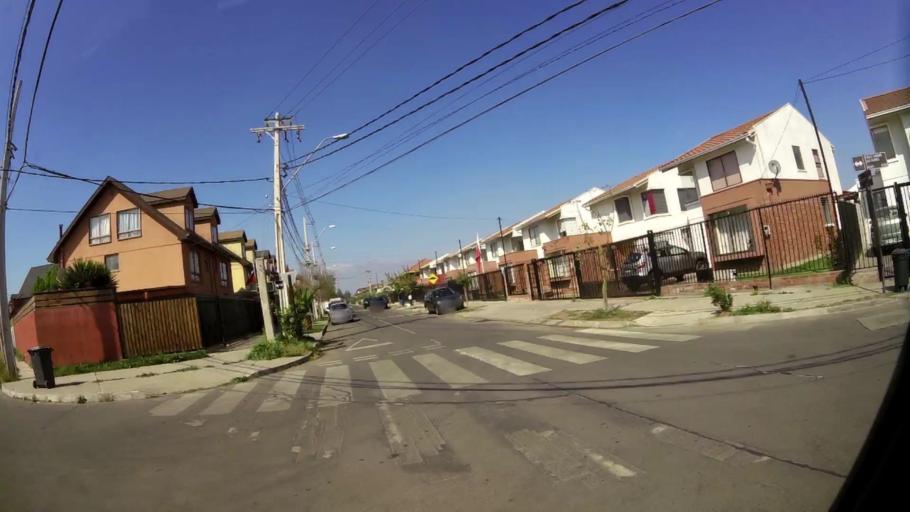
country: CL
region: Santiago Metropolitan
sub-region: Provincia de Santiago
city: Lo Prado
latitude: -33.4787
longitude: -70.7617
